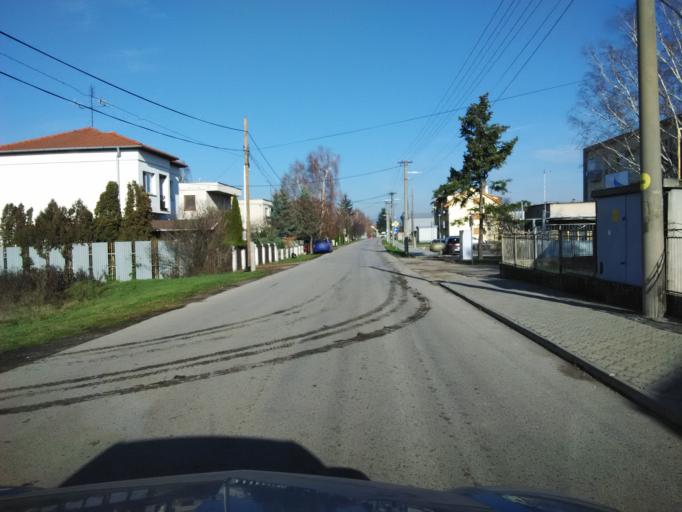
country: SK
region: Nitriansky
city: Tlmace
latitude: 48.2052
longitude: 18.5213
